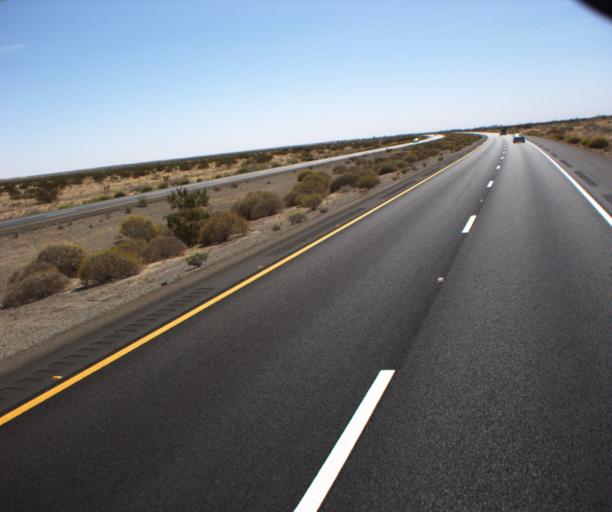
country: US
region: Arizona
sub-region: Yuma County
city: Fortuna Foothills
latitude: 32.6002
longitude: -114.5410
